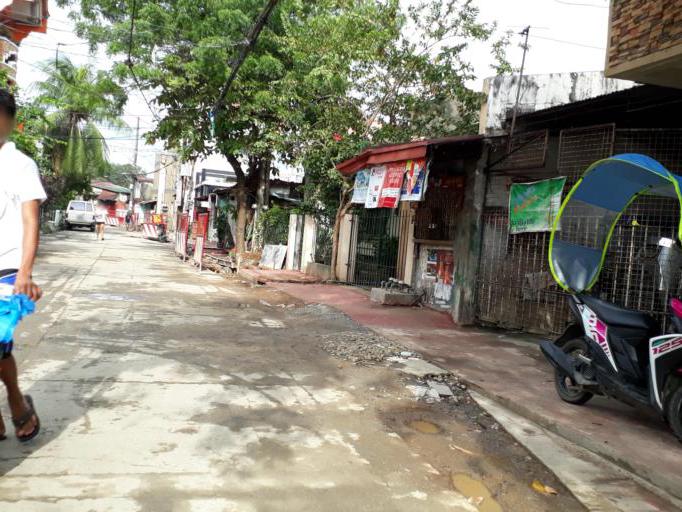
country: PH
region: Calabarzon
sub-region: Province of Rizal
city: Valenzuela
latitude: 14.6742
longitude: 120.9893
